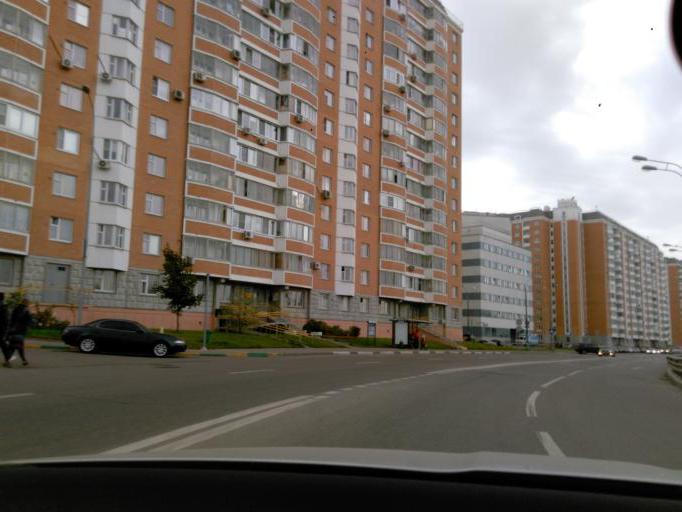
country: RU
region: Moscow
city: Severnyy
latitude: 55.9252
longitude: 37.5406
